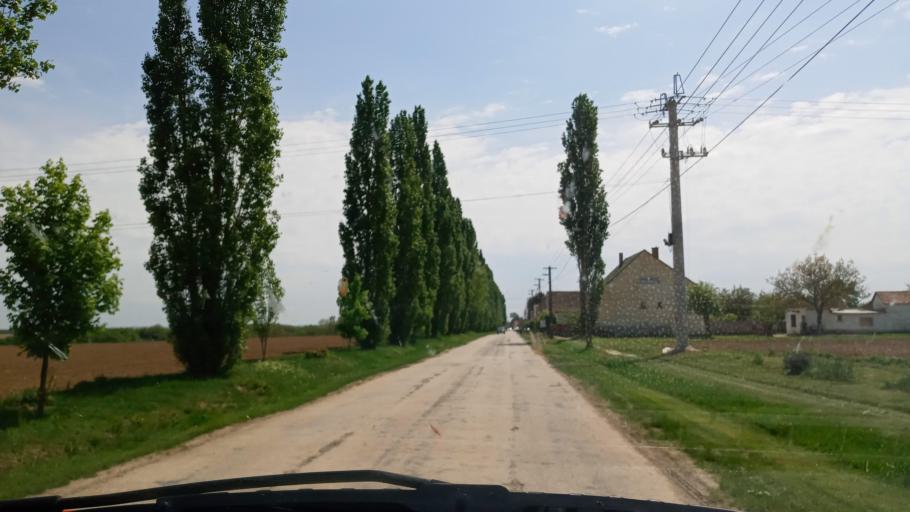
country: HU
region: Baranya
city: Villany
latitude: 45.8796
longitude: 18.5036
